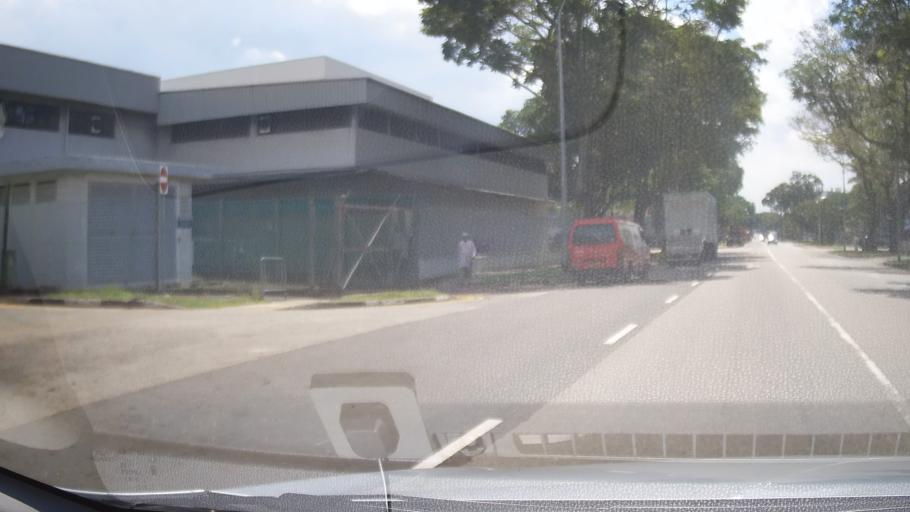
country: MY
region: Johor
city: Johor Bahru
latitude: 1.3315
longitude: 103.6936
